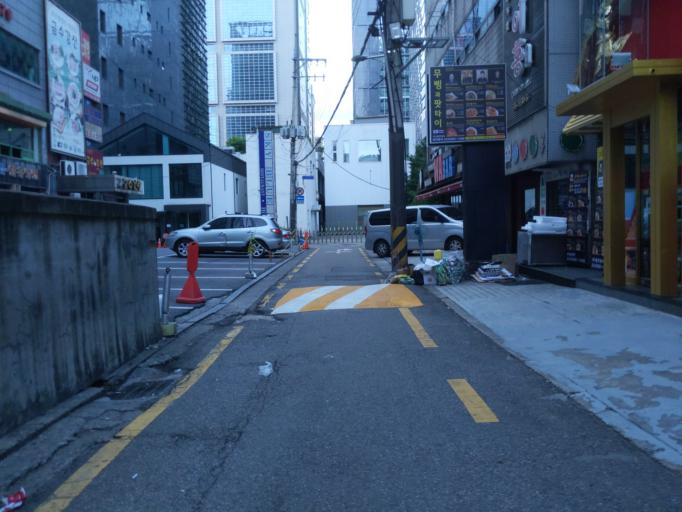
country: KR
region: Seoul
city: Seoul
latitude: 37.5085
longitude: 127.0582
